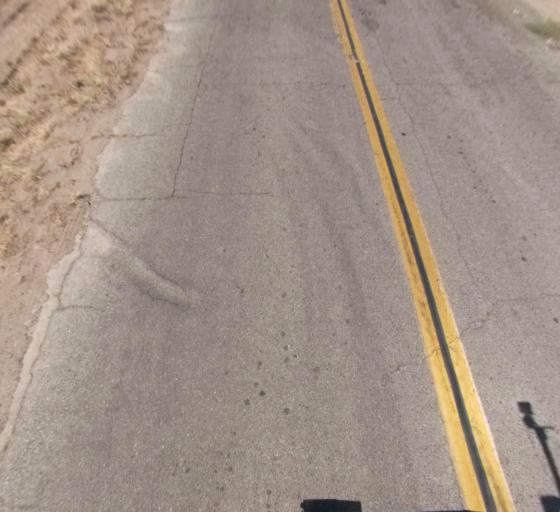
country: US
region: California
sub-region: Madera County
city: Parkwood
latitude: 36.8802
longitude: -120.0195
